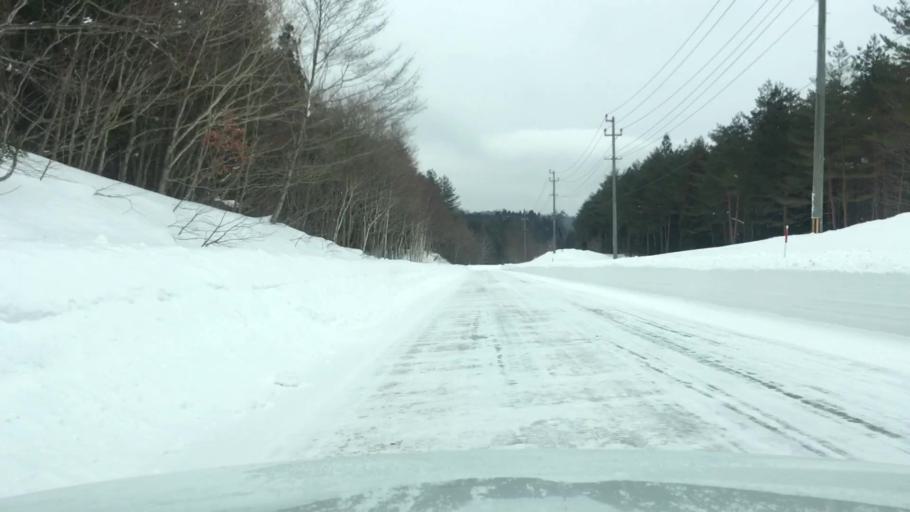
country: JP
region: Akita
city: Hanawa
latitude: 39.9873
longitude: 140.9996
